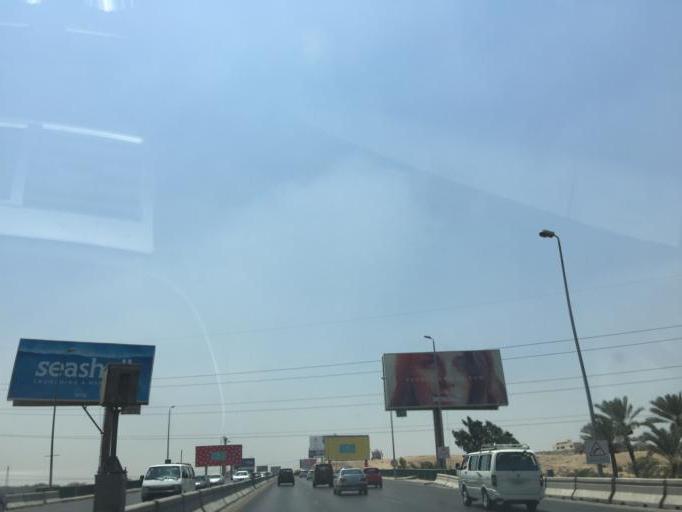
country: EG
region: Al Jizah
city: Awsim
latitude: 30.0587
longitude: 31.0816
